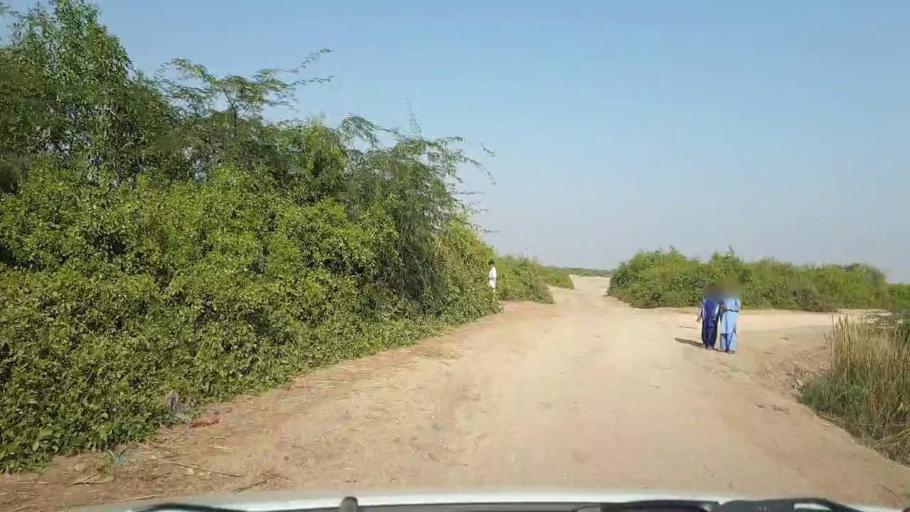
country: PK
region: Sindh
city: Mirpur Sakro
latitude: 24.6014
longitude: 67.6313
